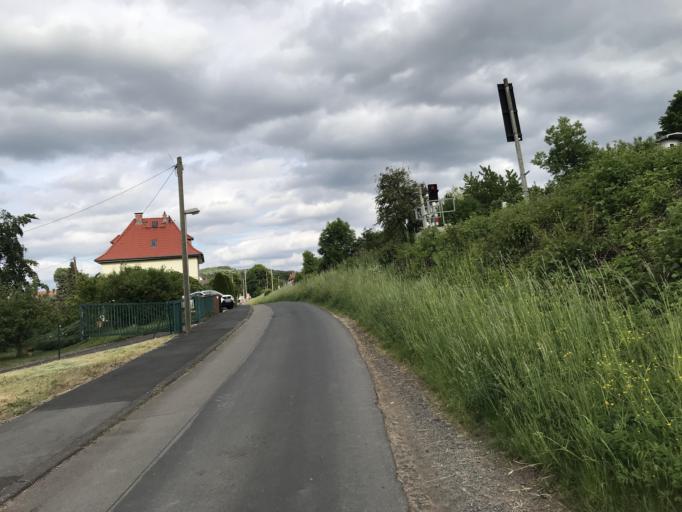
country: DE
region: Hesse
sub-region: Regierungsbezirk Kassel
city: Zierenberg
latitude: 51.3661
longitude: 9.2954
